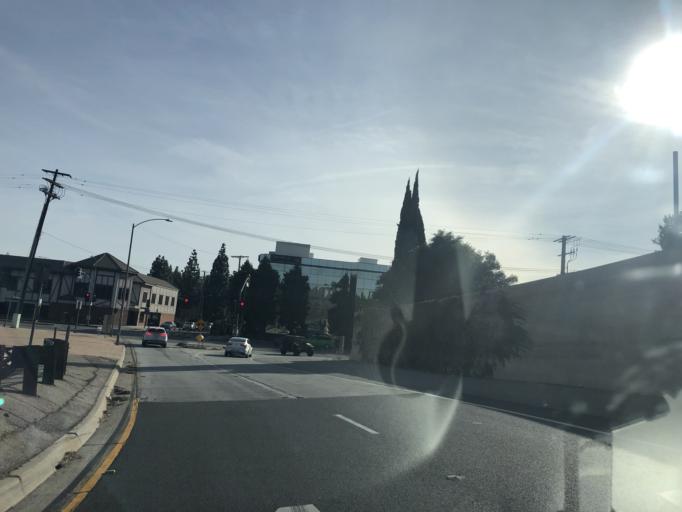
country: US
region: California
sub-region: Los Angeles County
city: San Fernando
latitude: 34.2580
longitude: -118.4735
